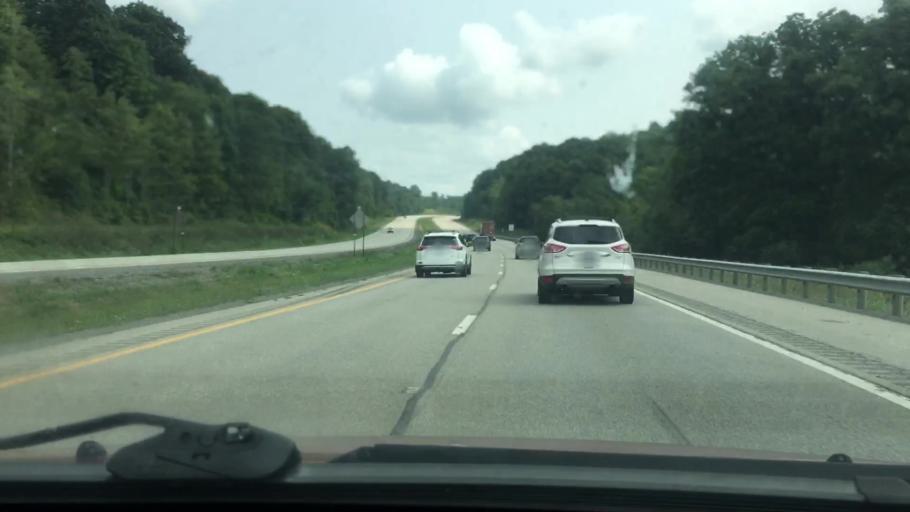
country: US
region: West Virginia
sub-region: Monongalia County
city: Cheat Lake
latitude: 39.6581
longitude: -79.6827
